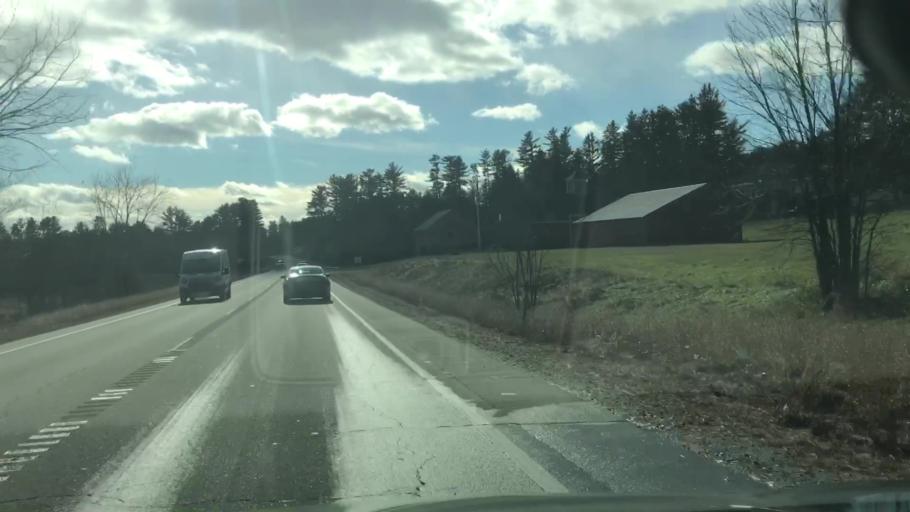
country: US
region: New Hampshire
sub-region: Merrimack County
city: Chichester
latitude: 43.2674
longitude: -71.3703
